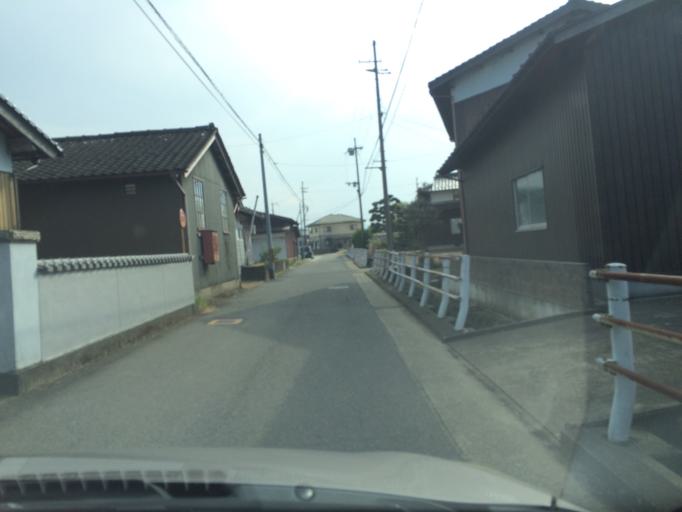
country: JP
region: Hyogo
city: Toyooka
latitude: 35.5219
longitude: 134.8271
